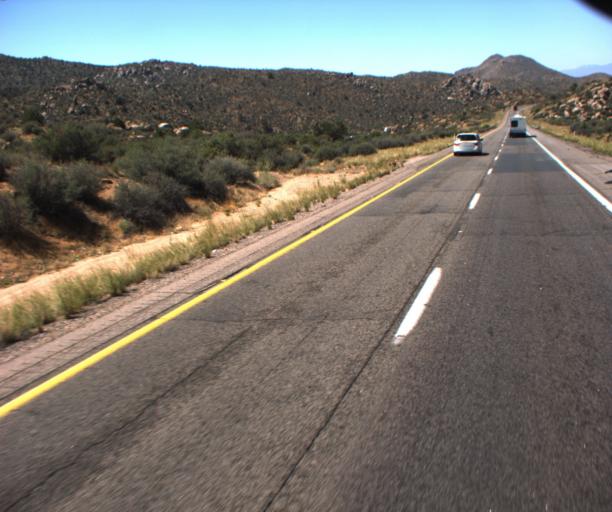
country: US
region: Arizona
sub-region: Mohave County
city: Peach Springs
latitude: 35.1781
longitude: -113.4963
